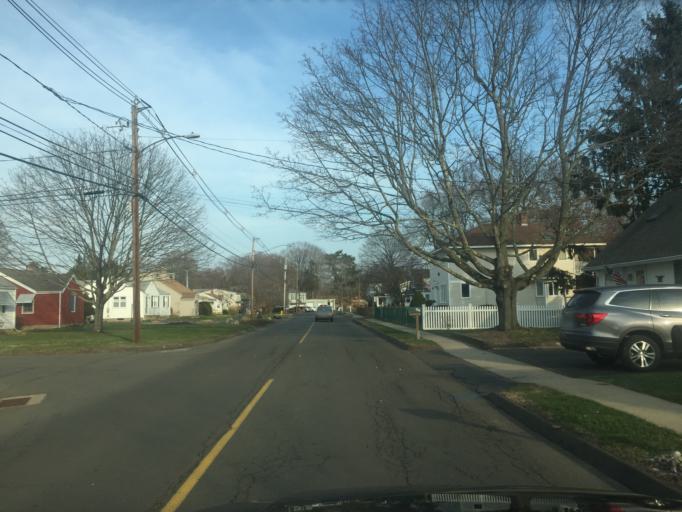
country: US
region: Connecticut
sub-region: New Haven County
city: Branford Center
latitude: 41.2700
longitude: -72.8073
